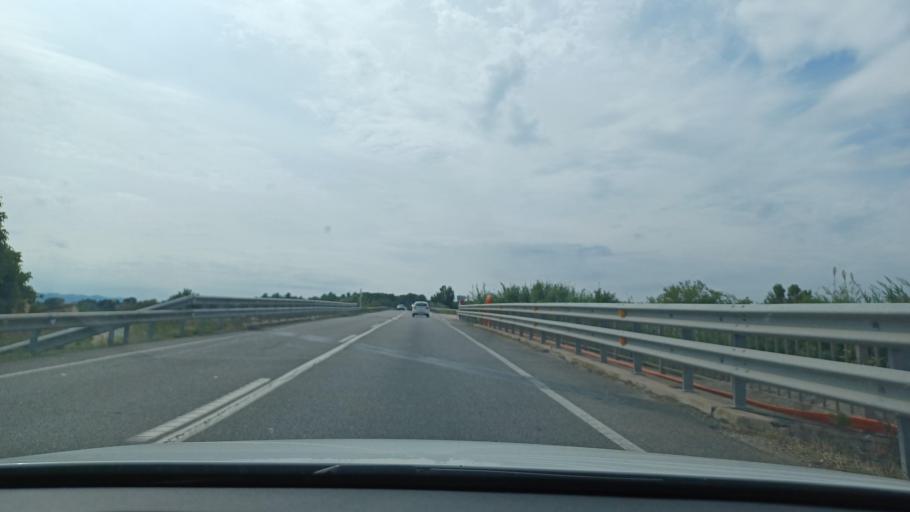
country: ES
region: Catalonia
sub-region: Provincia de Tarragona
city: Tortosa
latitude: 40.7939
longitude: 0.4972
